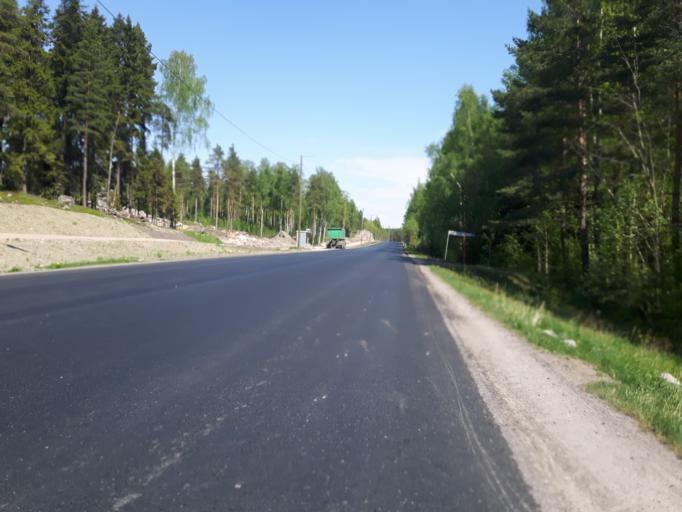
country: FI
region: Uusimaa
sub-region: Porvoo
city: Porvoo
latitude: 60.3611
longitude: 25.5392
